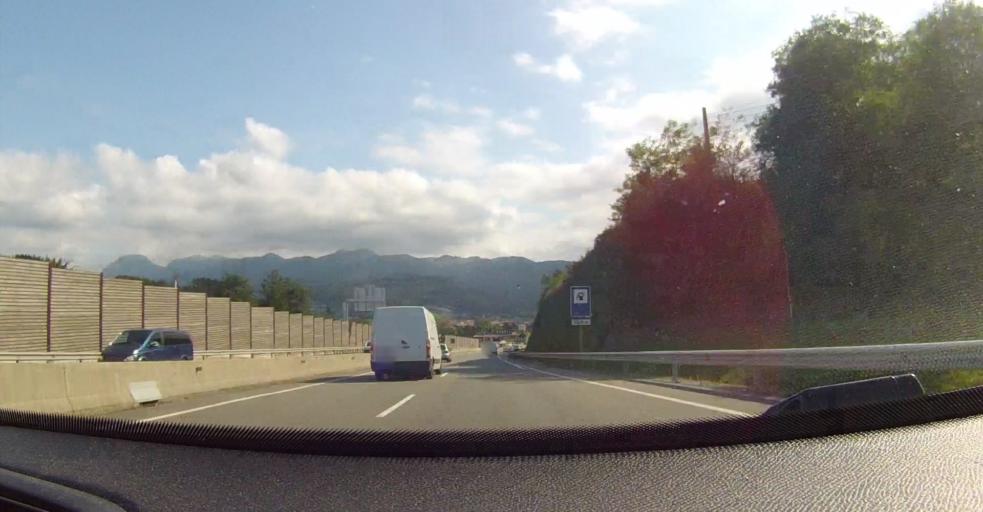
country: ES
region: Basque Country
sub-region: Bizkaia
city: Amorebieta
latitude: 43.2325
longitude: -2.7285
